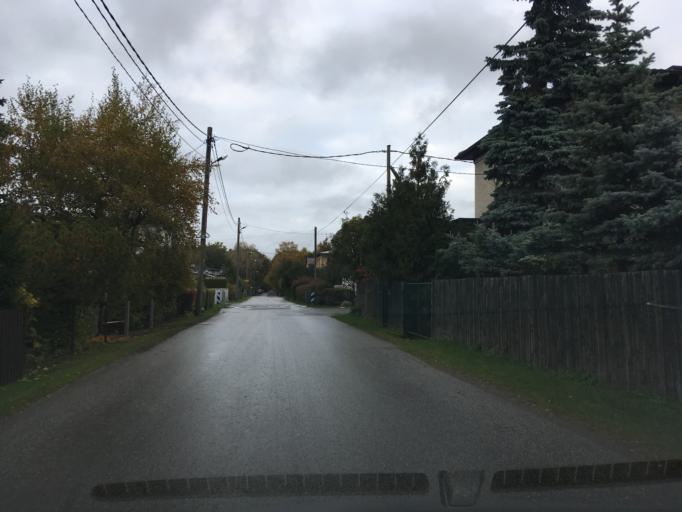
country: EE
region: Harju
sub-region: Tallinna linn
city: Kose
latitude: 59.4551
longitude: 24.8510
